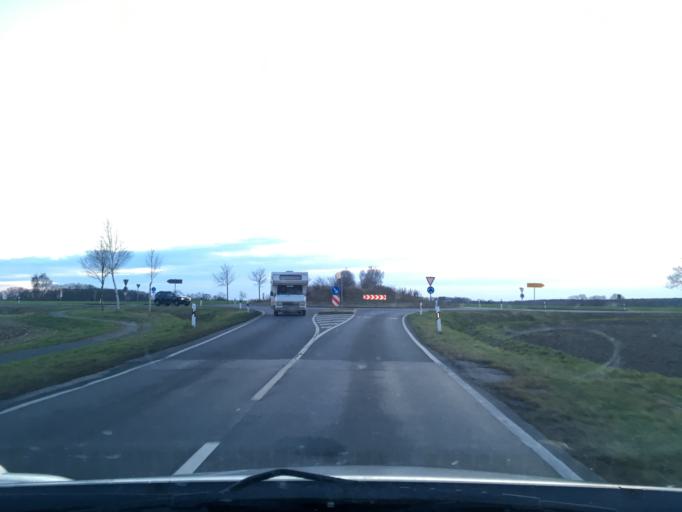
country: DE
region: Lower Saxony
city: Waddeweitz
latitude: 52.9887
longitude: 10.9809
